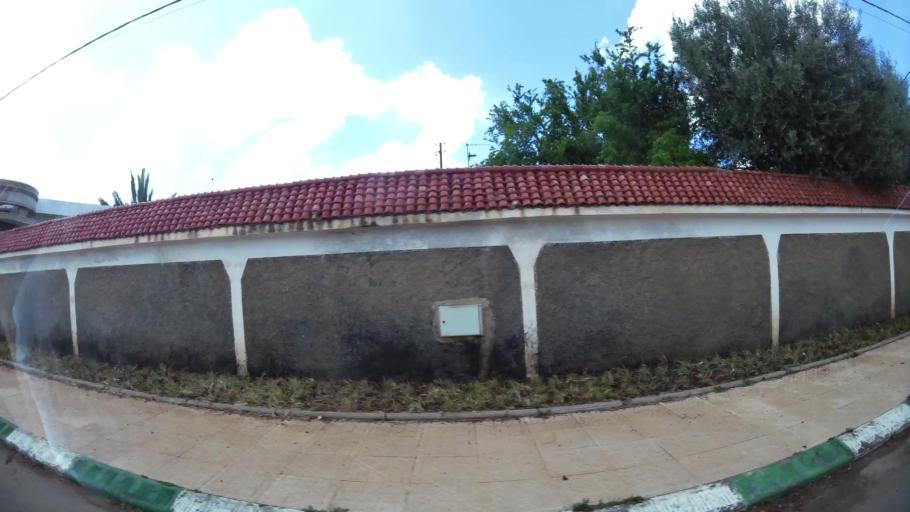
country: MA
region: Grand Casablanca
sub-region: Mediouna
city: Mediouna
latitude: 33.3855
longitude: -7.5403
